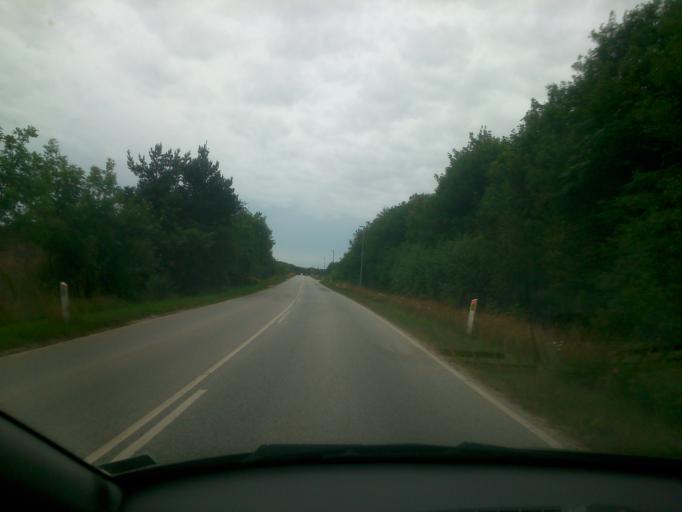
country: DK
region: South Denmark
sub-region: Esbjerg Kommune
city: Esbjerg
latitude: 55.5302
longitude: 8.4394
